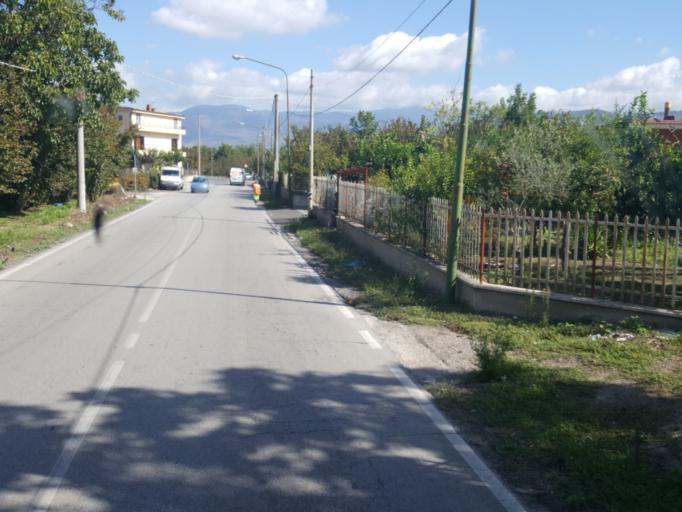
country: IT
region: Campania
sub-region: Provincia di Napoli
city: Piazzolla
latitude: 40.8943
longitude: 14.5231
